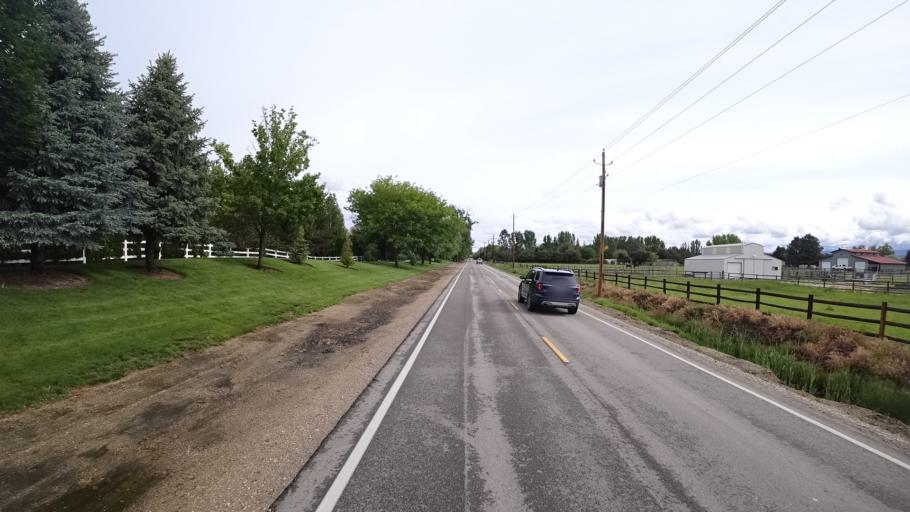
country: US
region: Idaho
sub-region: Ada County
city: Eagle
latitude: 43.7122
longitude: -116.3792
